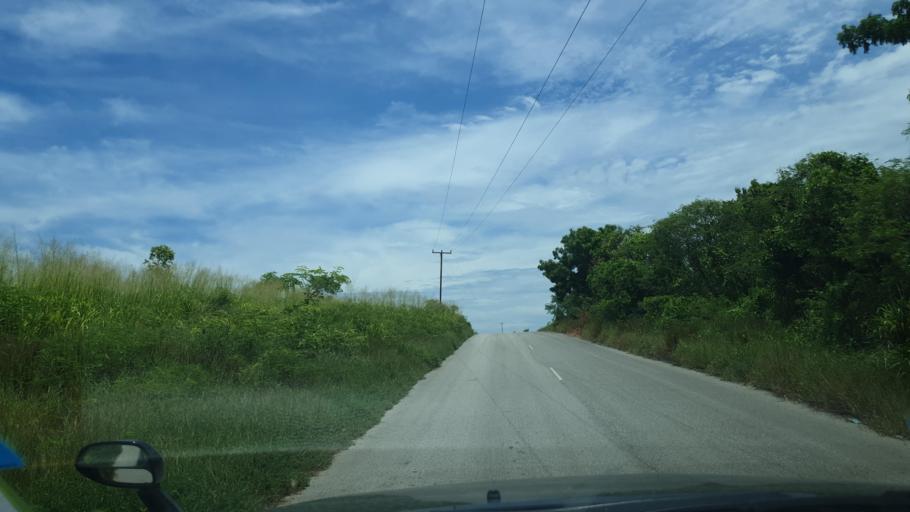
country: PG
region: National Capital
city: Port Moresby
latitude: -9.4300
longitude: 147.0542
